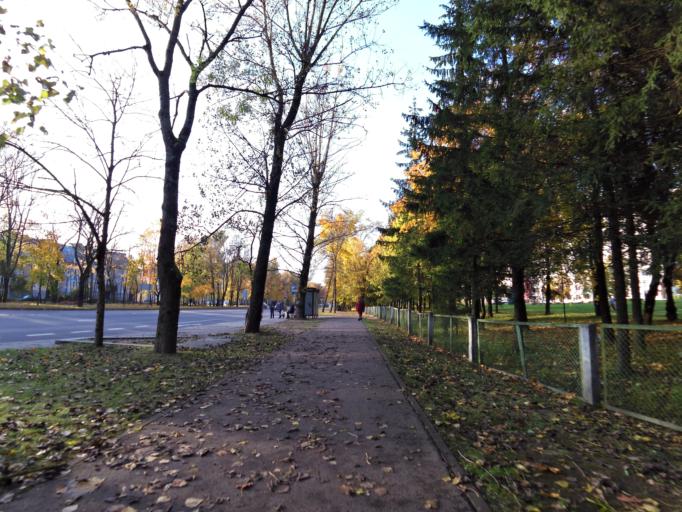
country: LT
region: Vilnius County
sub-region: Vilnius
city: Fabijoniskes
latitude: 54.7501
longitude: 25.2780
